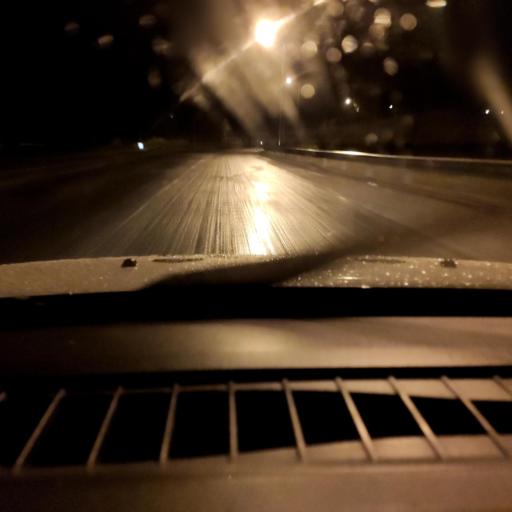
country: RU
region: Udmurtiya
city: Khokhryaki
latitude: 57.1812
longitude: 53.1579
